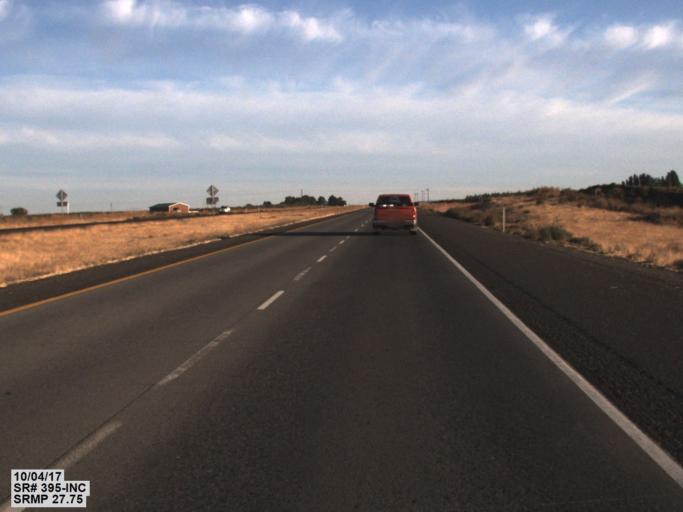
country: US
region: Washington
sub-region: Franklin County
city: Pasco
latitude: 46.3234
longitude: -119.0928
